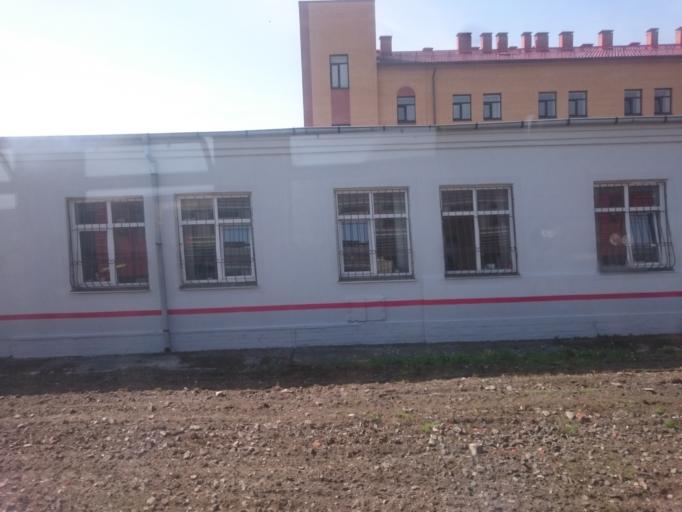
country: RU
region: Kaliningrad
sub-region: Gorod Kaliningrad
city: Kaliningrad
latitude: 54.6955
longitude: 20.4942
